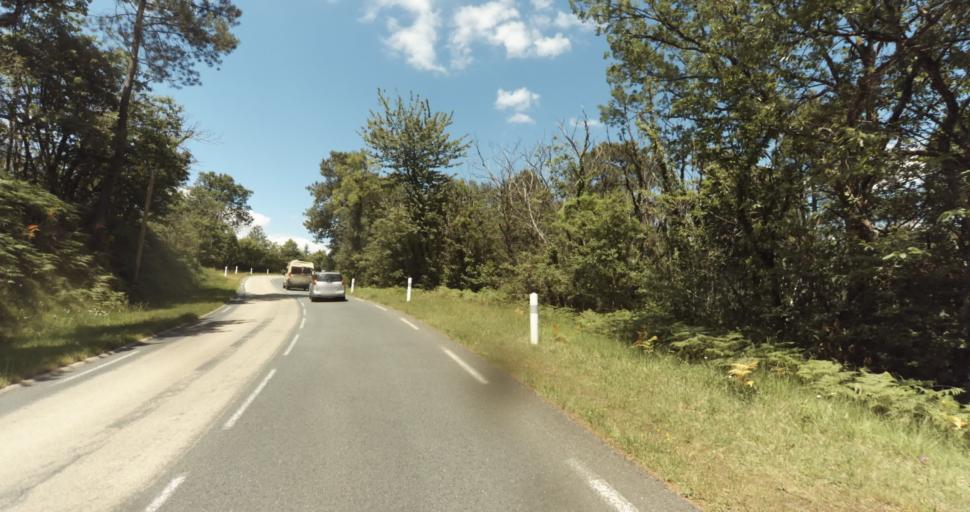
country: FR
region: Aquitaine
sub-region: Departement de la Dordogne
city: Le Bugue
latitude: 44.8401
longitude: 0.8700
